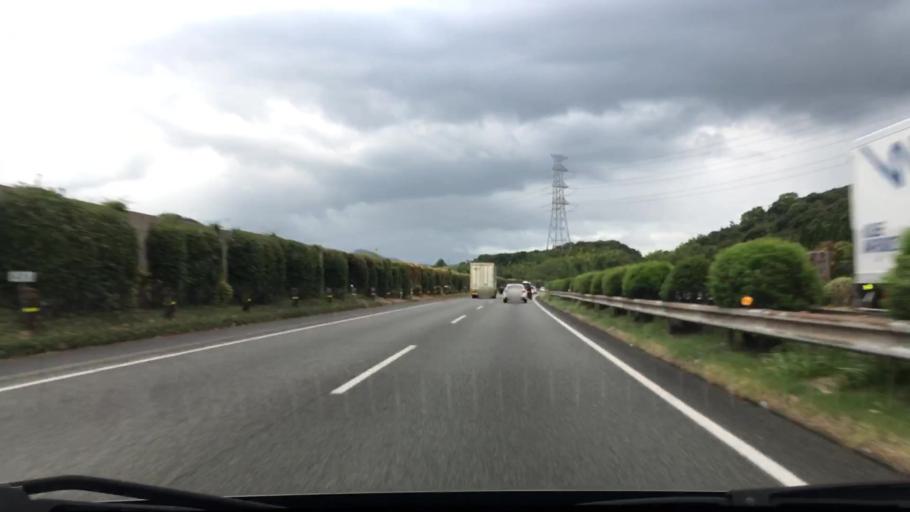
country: JP
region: Fukuoka
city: Miyata
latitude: 33.7497
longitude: 130.5882
